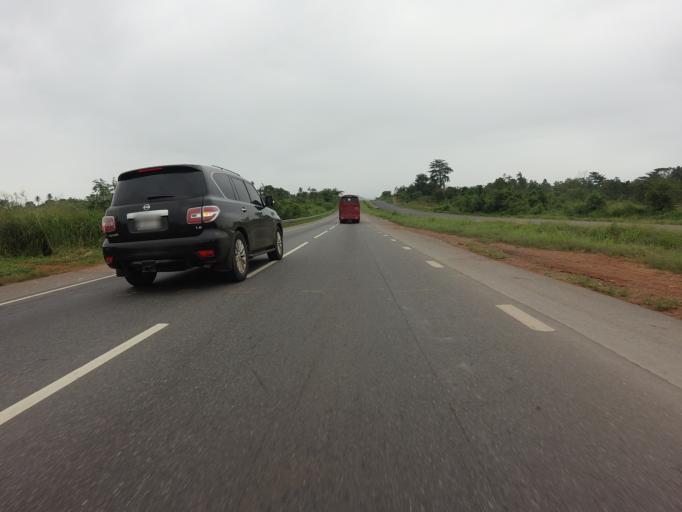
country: GH
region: Eastern
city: Suhum
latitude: 6.0739
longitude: -0.4699
